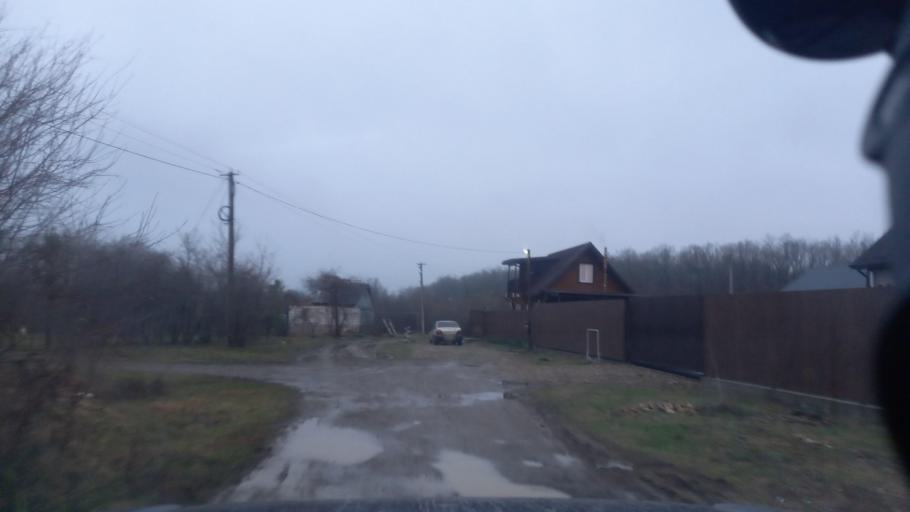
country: RU
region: Krasnodarskiy
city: Saratovskaya
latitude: 44.6454
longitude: 39.3044
